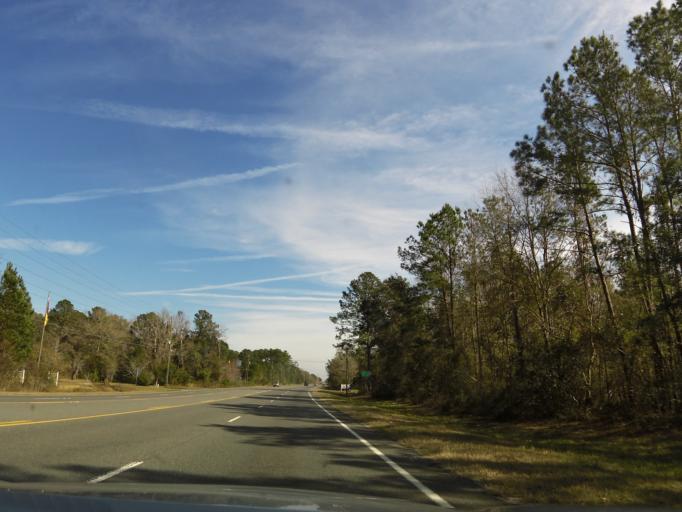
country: US
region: Georgia
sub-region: Brantley County
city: Nahunta
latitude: 31.2293
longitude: -81.7883
